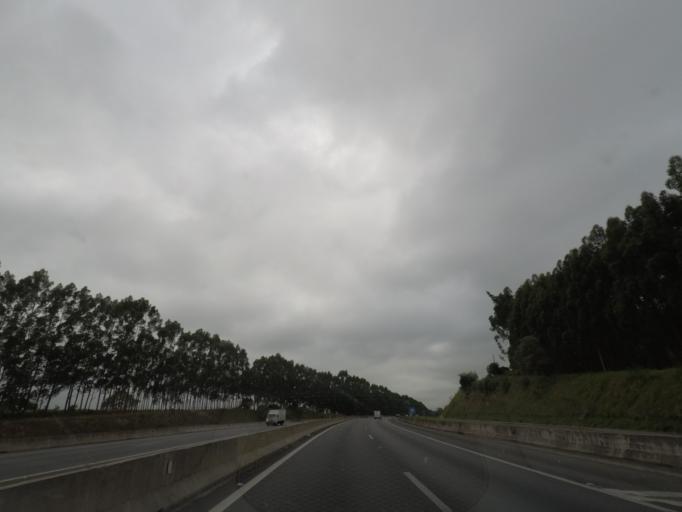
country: BR
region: Sao Paulo
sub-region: Itatiba
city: Itatiba
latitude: -22.9355
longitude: -46.8841
